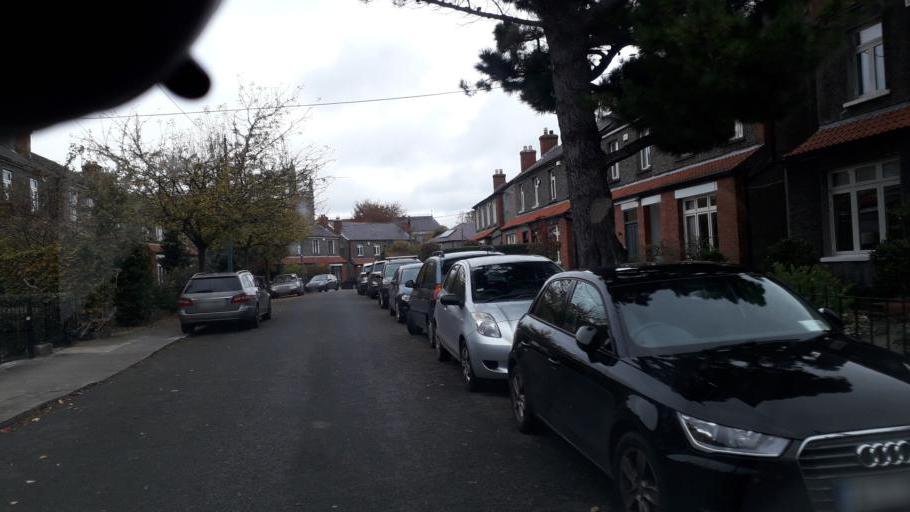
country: IE
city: Milltown
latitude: 53.3167
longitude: -6.2527
